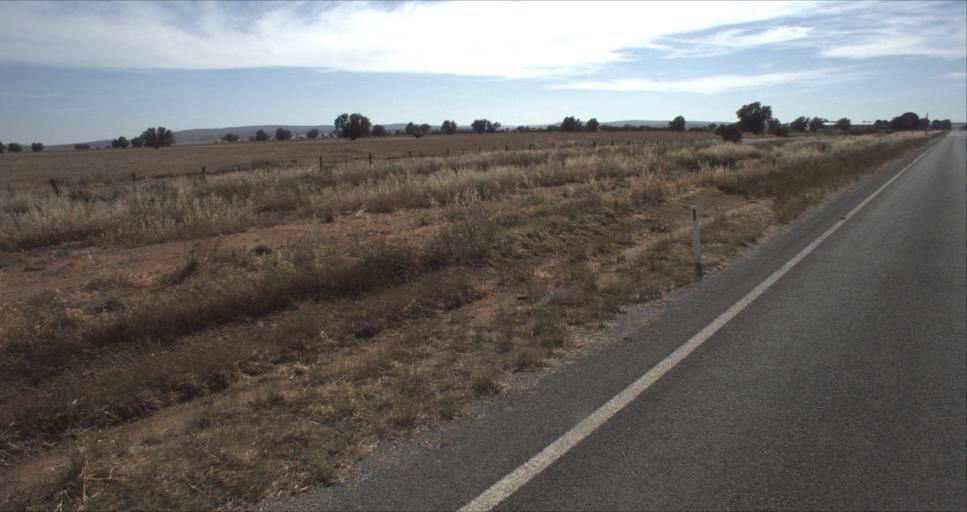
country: AU
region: New South Wales
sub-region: Leeton
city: Leeton
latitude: -34.5573
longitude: 146.4563
